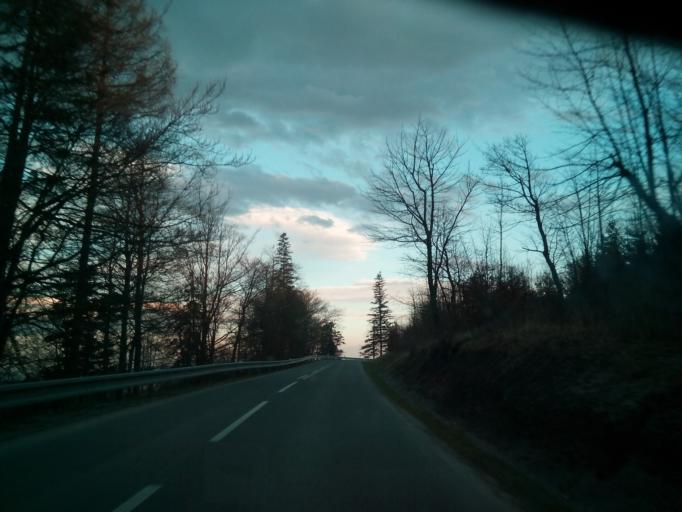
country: SK
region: Presovsky
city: Spisska Bela
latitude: 49.2887
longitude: 20.4305
